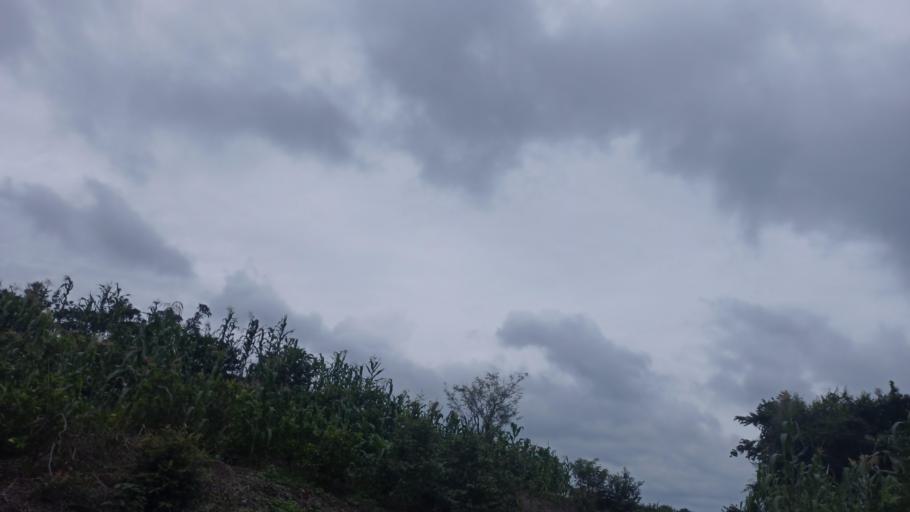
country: MX
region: Puebla
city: Espinal
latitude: 20.2974
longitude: -97.4008
